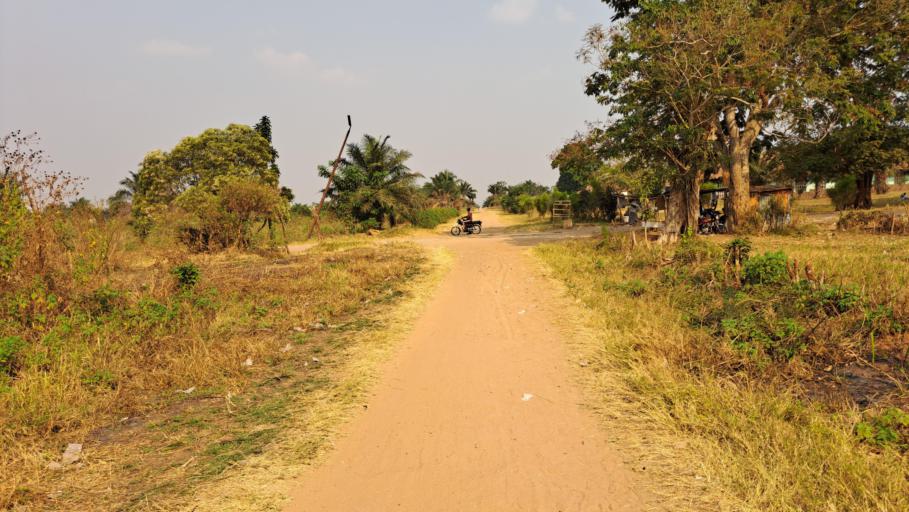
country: CD
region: Kasai-Oriental
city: Mbuji-Mayi
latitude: -6.1408
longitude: 23.5923
